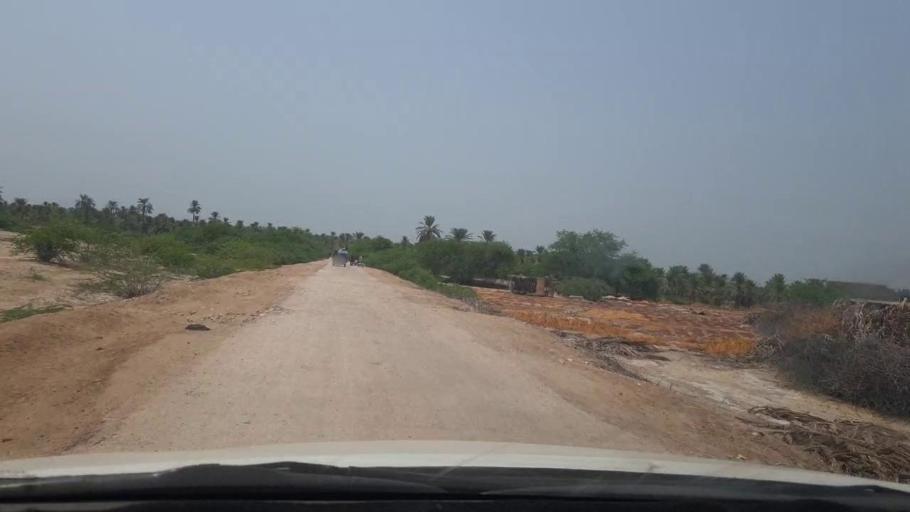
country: PK
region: Sindh
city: Khairpur
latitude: 27.4994
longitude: 68.8817
